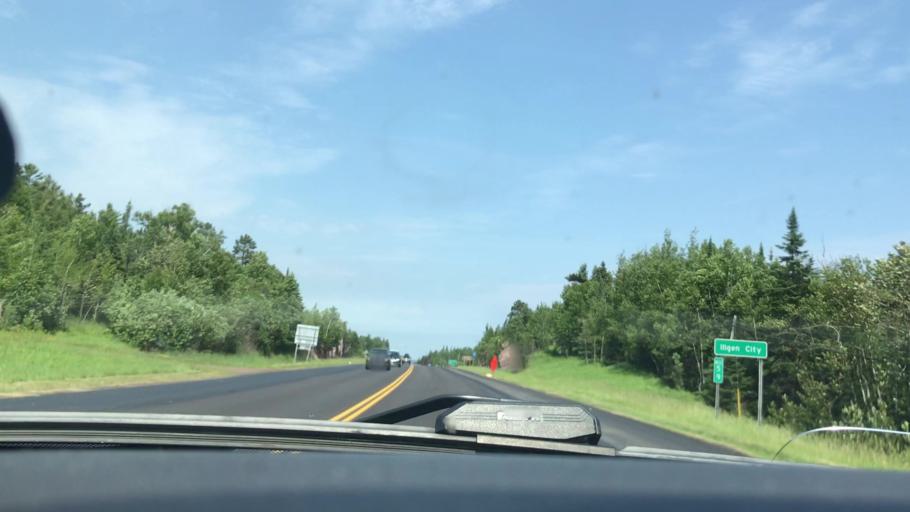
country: US
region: Minnesota
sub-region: Lake County
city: Silver Bay
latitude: 47.3432
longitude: -91.1915
